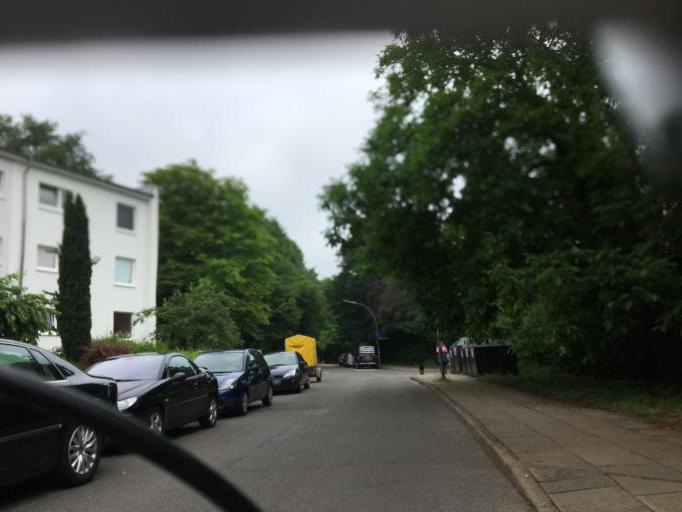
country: DE
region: Hamburg
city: Eidelstedt
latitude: 53.5693
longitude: 9.8703
